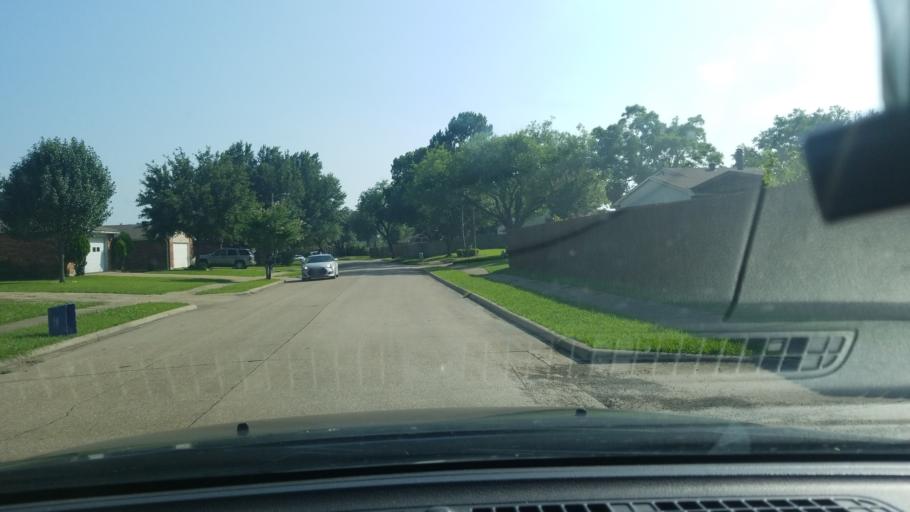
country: US
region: Texas
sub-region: Dallas County
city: Sunnyvale
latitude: 32.8186
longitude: -96.6026
